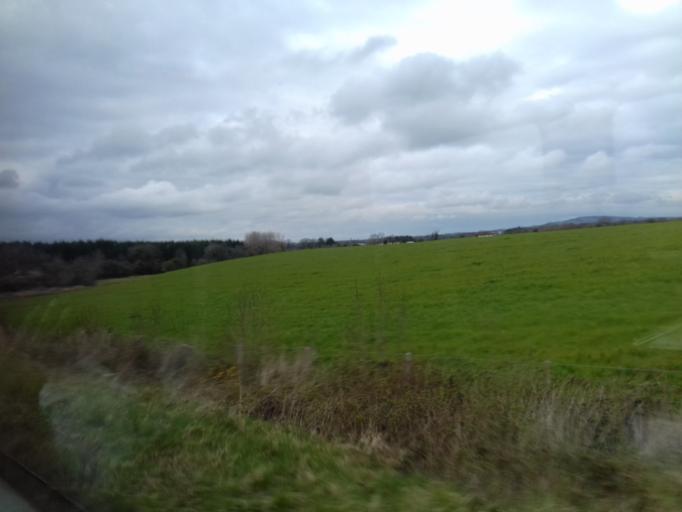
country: IE
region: Leinster
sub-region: An Longfort
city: Longford
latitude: 53.7157
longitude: -7.7534
